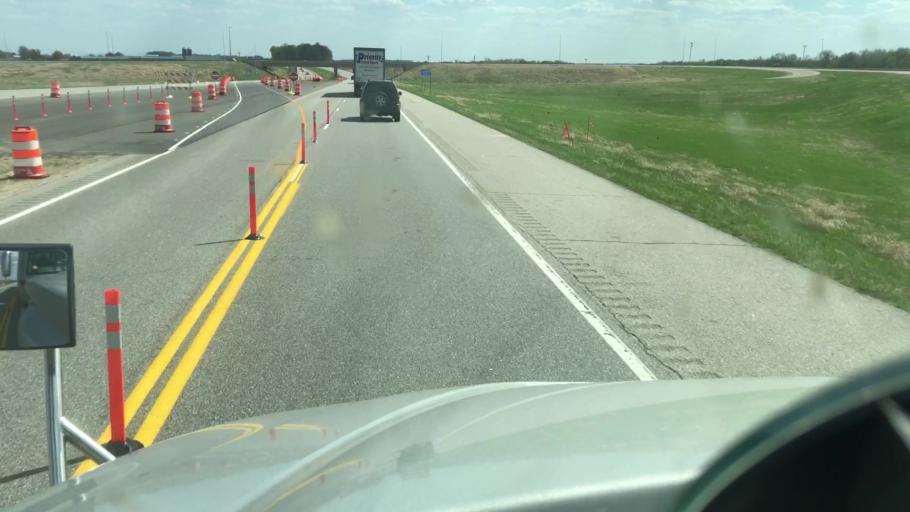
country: US
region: Minnesota
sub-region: Le Sueur County
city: Le Sueur
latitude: 44.5467
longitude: -93.8496
